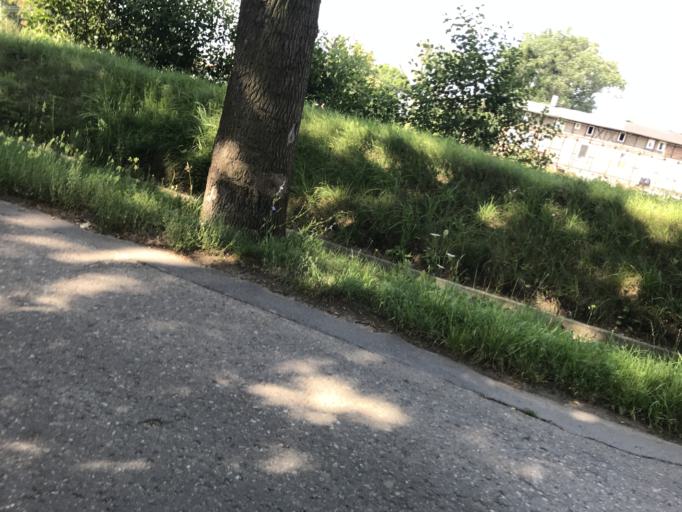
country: PL
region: Pomeranian Voivodeship
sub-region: Gdansk
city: Gdansk
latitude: 54.3322
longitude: 18.6575
